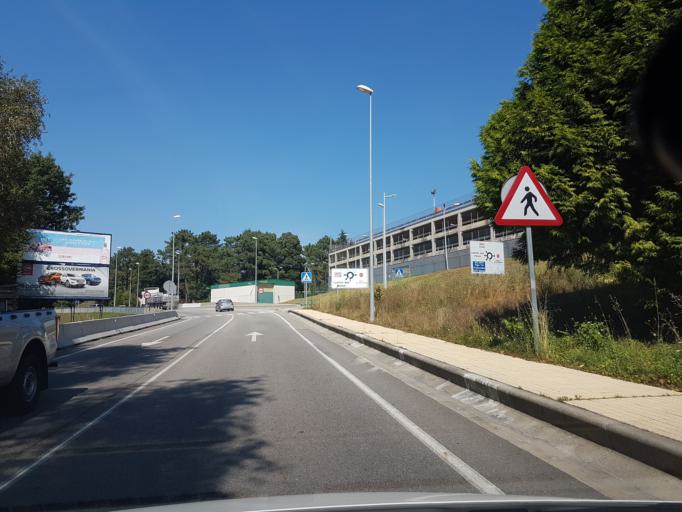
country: ES
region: Galicia
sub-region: Provincia de Pontevedra
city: Redondela
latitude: 42.2273
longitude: -8.6330
